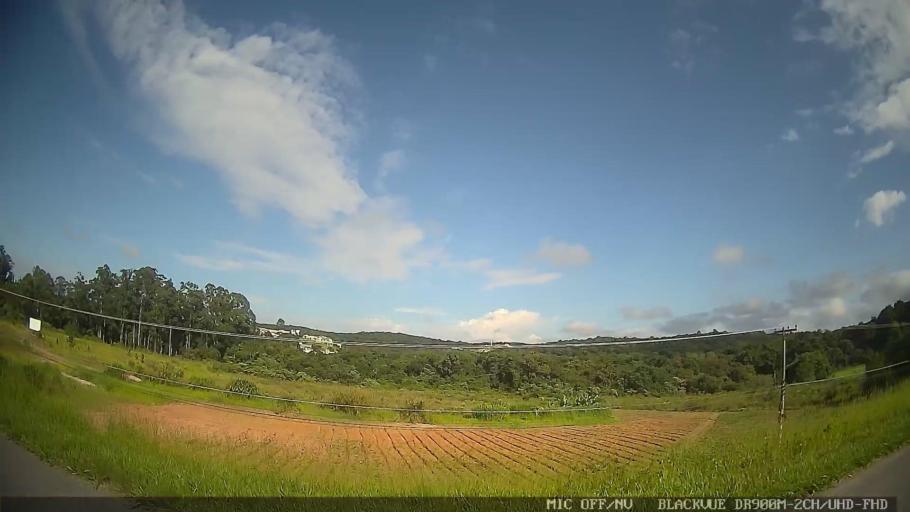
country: BR
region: Sao Paulo
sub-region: Jarinu
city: Jarinu
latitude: -23.0615
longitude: -46.6823
